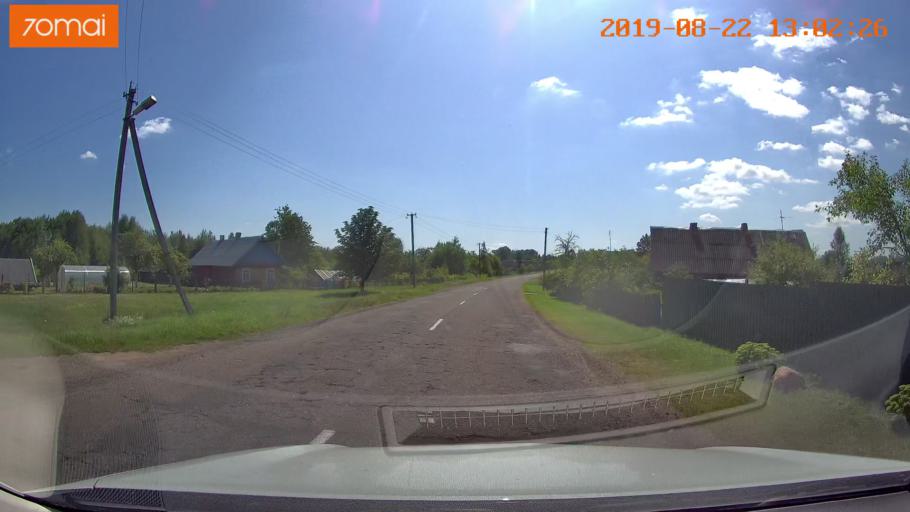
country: BY
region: Minsk
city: Prawdzinski
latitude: 53.3890
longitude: 27.8253
